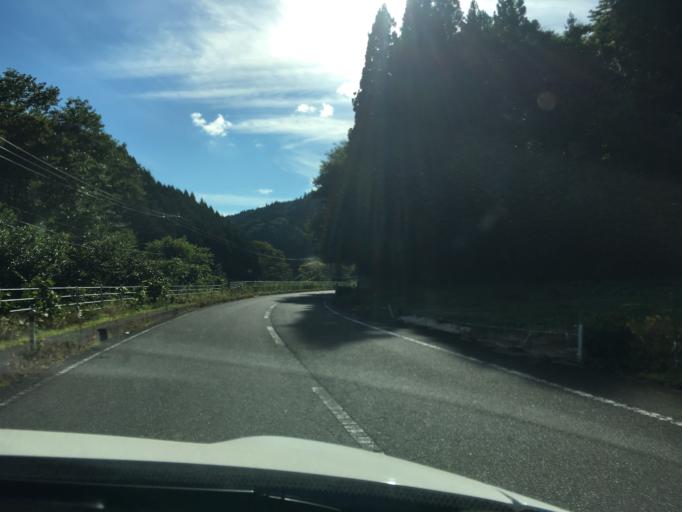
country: JP
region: Fukushima
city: Ishikawa
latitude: 37.1219
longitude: 140.5704
